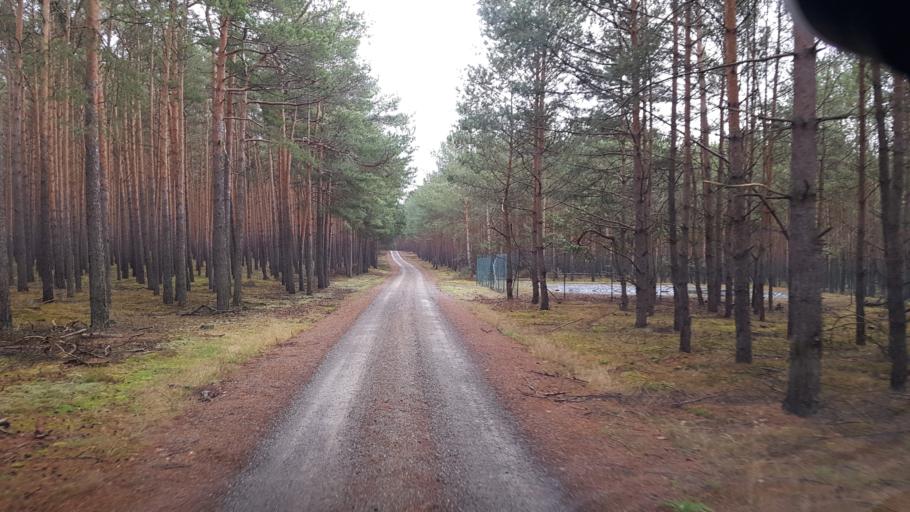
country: DE
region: Brandenburg
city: Hohenbucko
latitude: 51.7482
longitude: 13.4310
